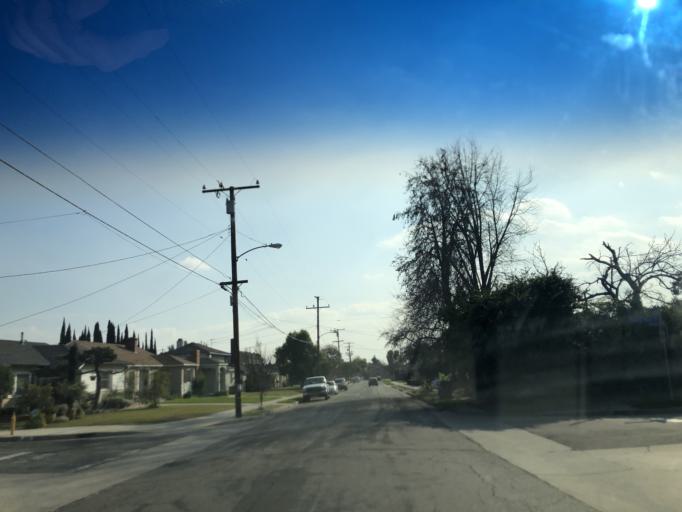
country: US
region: California
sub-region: Los Angeles County
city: East San Gabriel
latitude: 34.1083
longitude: -118.0865
